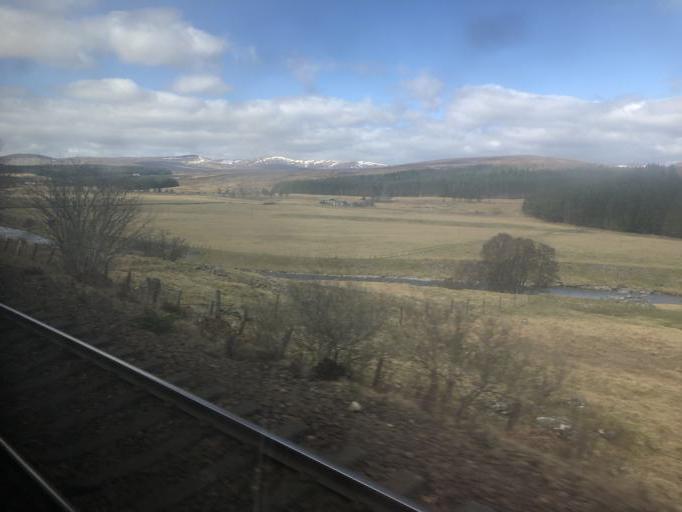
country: GB
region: Scotland
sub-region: Perth and Kinross
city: Aberfeldy
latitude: 56.7982
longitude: -4.0478
